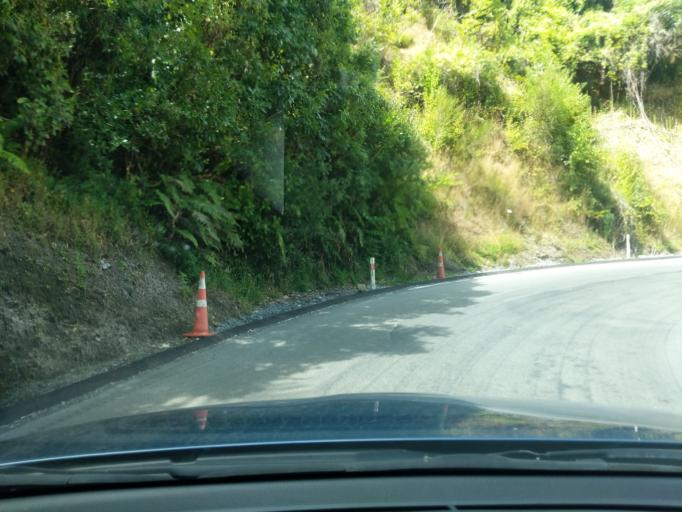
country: NZ
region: Tasman
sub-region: Tasman District
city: Motueka
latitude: -41.0487
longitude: 172.9612
